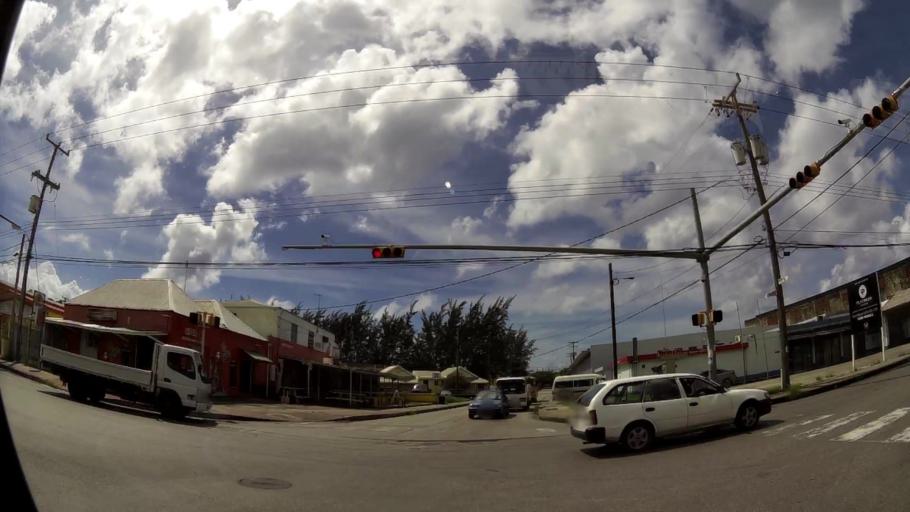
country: BB
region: Saint Michael
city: Bridgetown
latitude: 13.0999
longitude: -59.6224
